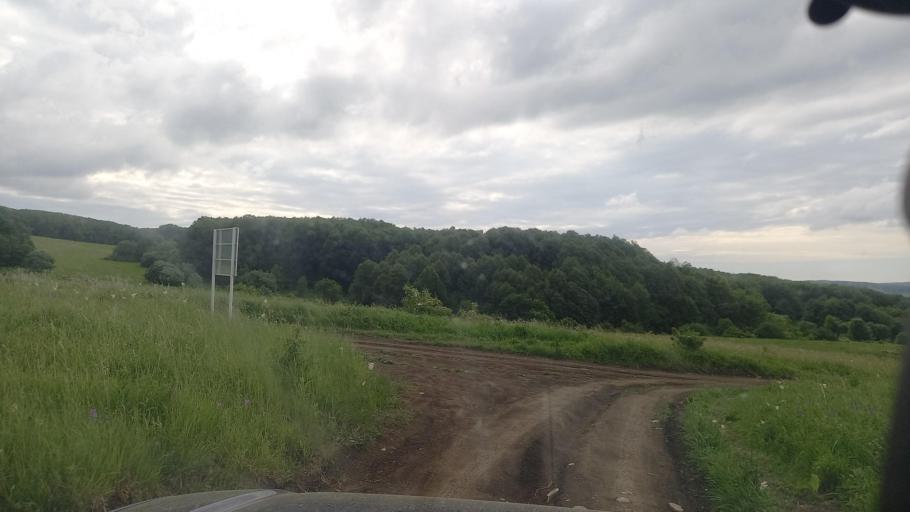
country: RU
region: Krasnodarskiy
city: Peredovaya
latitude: 44.0554
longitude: 41.3631
